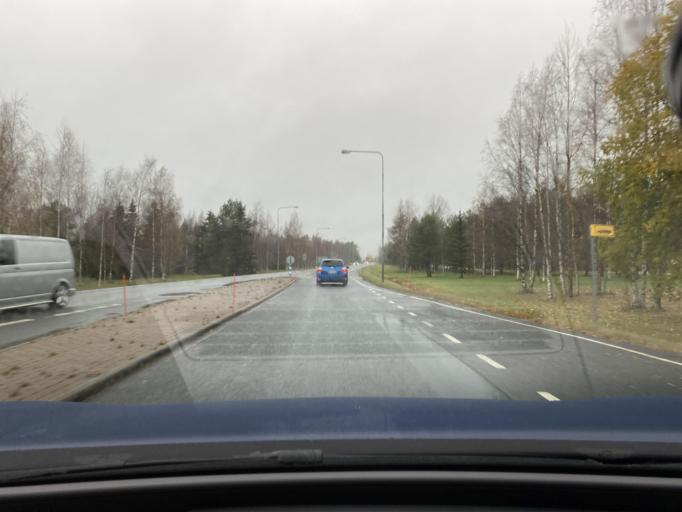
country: FI
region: Varsinais-Suomi
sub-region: Loimaa
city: Loimaa
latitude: 60.8606
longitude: 23.0267
